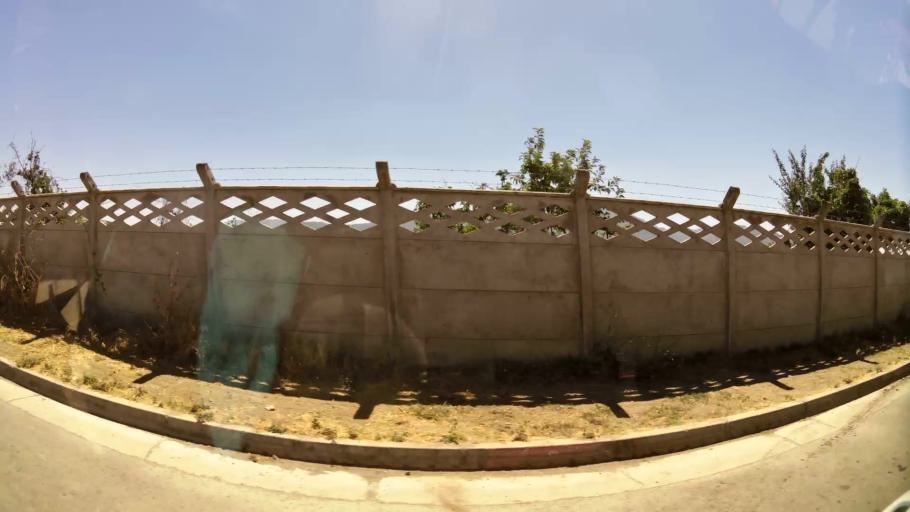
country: CL
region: O'Higgins
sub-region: Provincia de Colchagua
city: Chimbarongo
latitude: -34.5743
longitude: -70.9771
